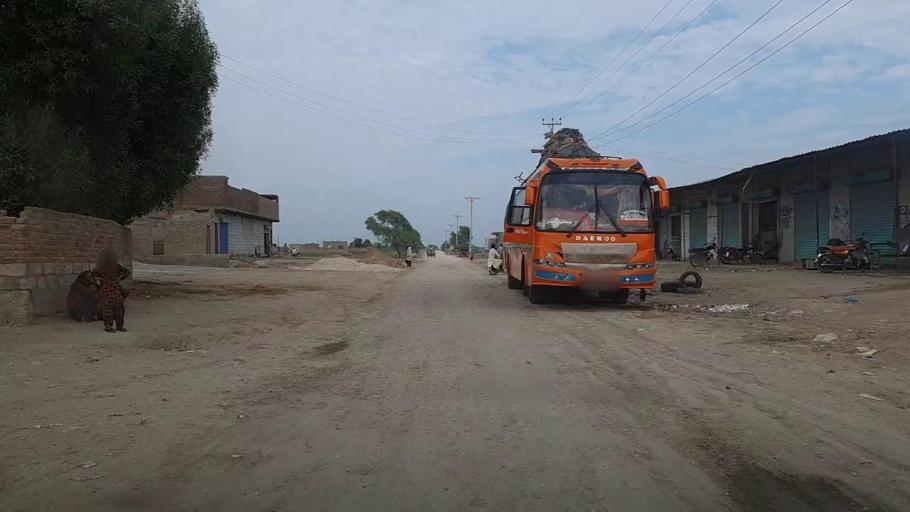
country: PK
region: Sindh
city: Thul
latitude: 28.2451
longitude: 68.7861
